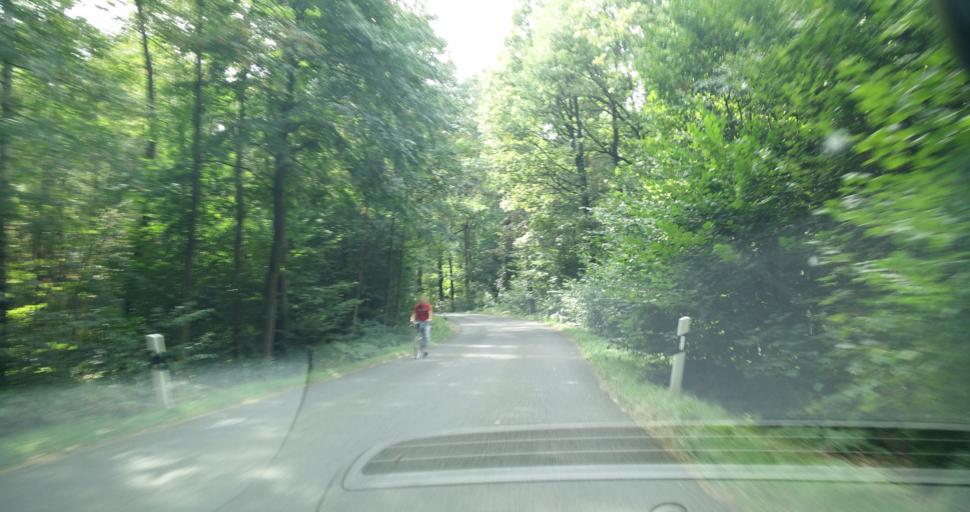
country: DE
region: Saxony
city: Bad Lausick
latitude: 51.1486
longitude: 12.6760
